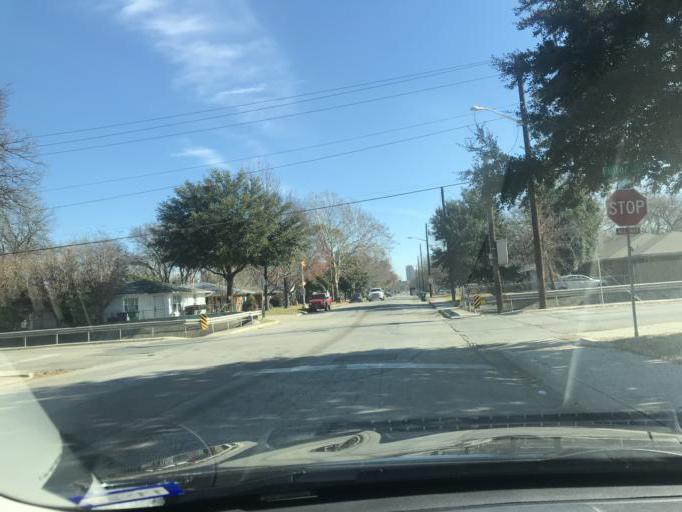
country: US
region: Texas
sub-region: Denton County
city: Denton
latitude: 33.2255
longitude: -97.1435
